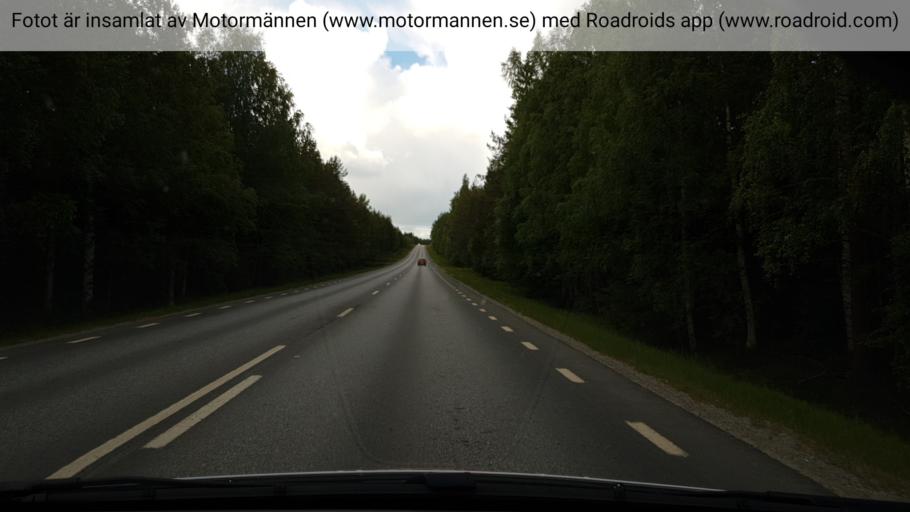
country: SE
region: Vaesterbotten
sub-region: Vannas Kommun
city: Vannasby
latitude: 64.0365
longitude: 20.0113
